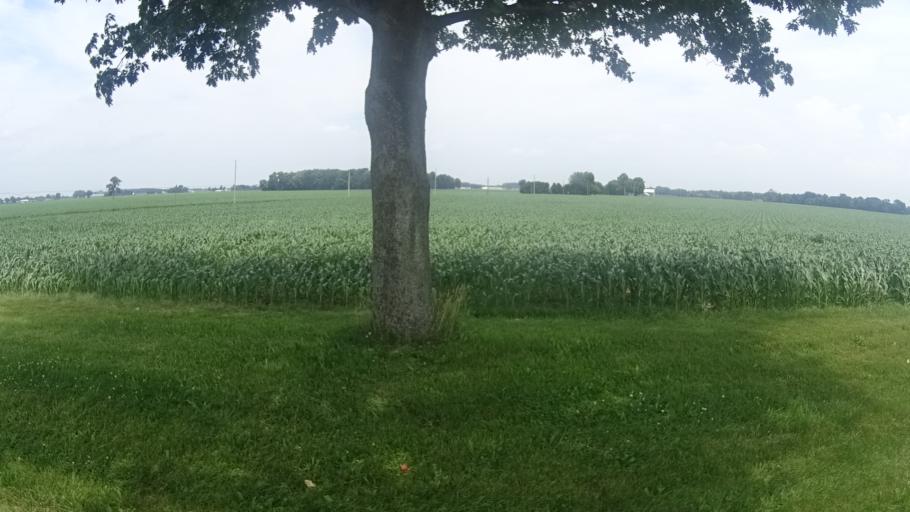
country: US
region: Ohio
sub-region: Erie County
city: Milan
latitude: 41.3066
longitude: -82.6335
